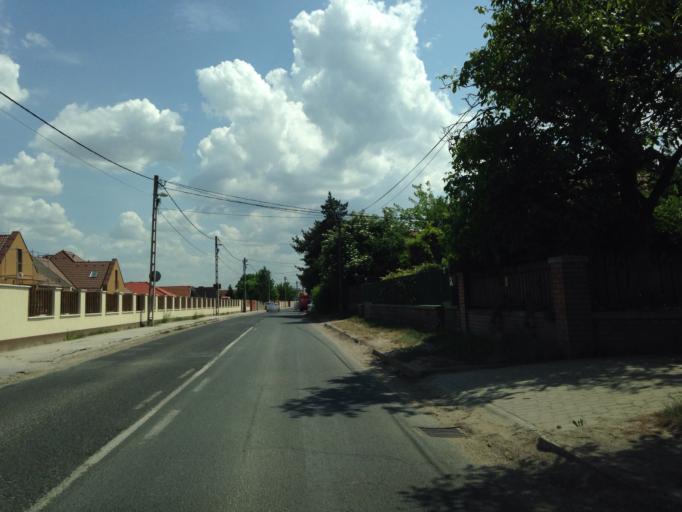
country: HU
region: Pest
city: Szentendre
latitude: 47.6778
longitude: 19.0674
